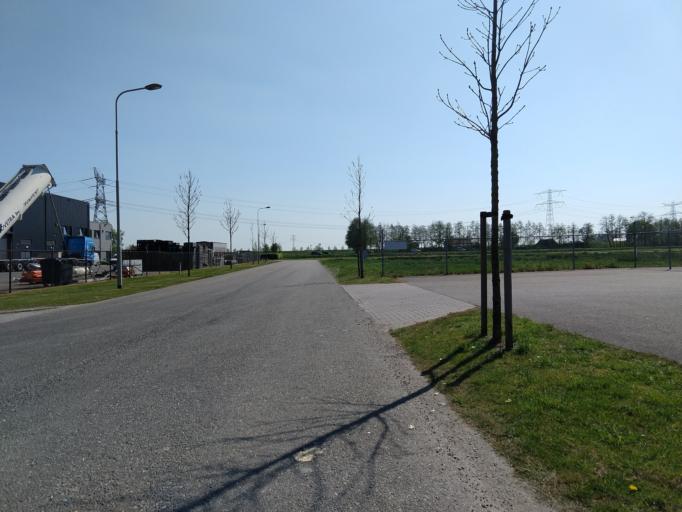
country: NL
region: Zeeland
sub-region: Gemeente Reimerswaal
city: Yerseke
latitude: 51.4687
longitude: 3.9832
